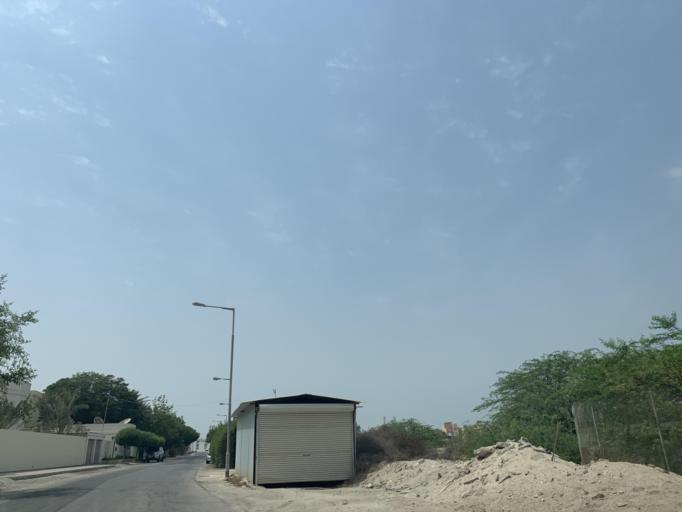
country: BH
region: Manama
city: Jidd Hafs
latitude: 26.2056
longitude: 50.4873
